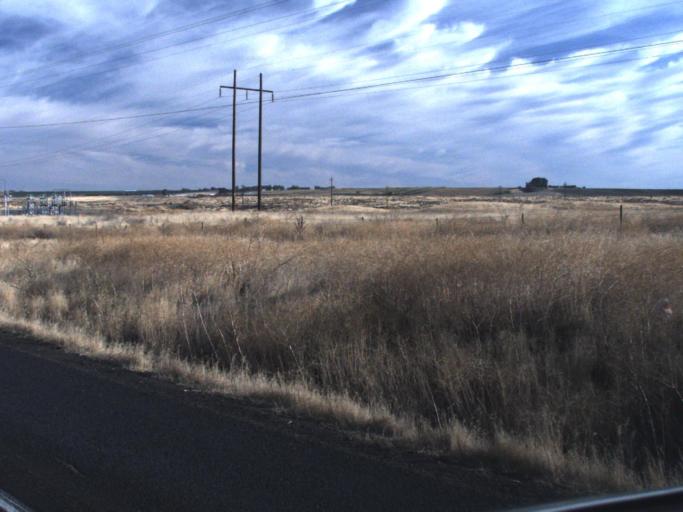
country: US
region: Washington
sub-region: Franklin County
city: Connell
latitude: 46.6616
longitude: -119.0063
